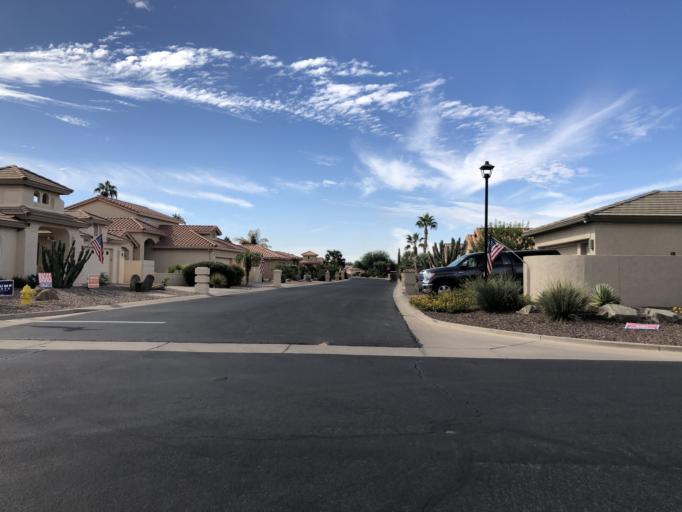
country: US
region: Arizona
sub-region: Maricopa County
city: Sun Lakes
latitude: 33.2274
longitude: -111.8832
